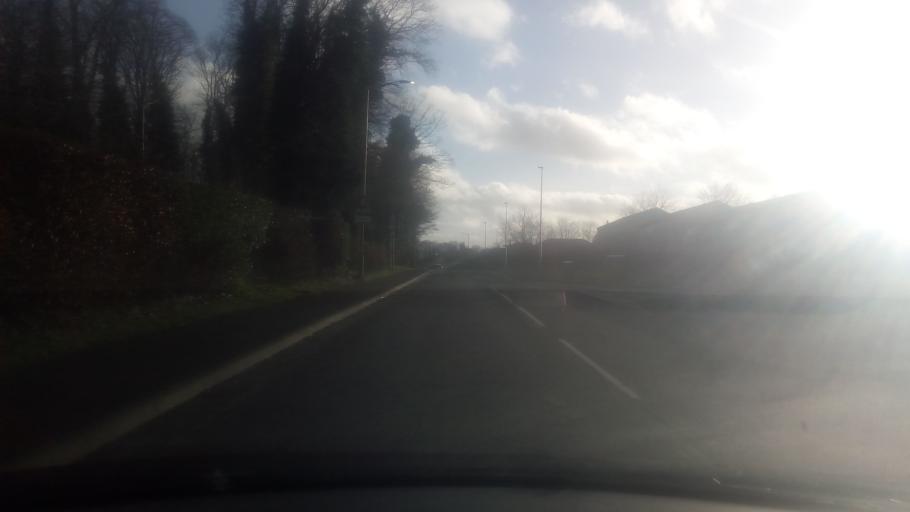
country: GB
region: Scotland
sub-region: The Scottish Borders
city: Kelso
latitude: 55.6087
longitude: -2.4278
